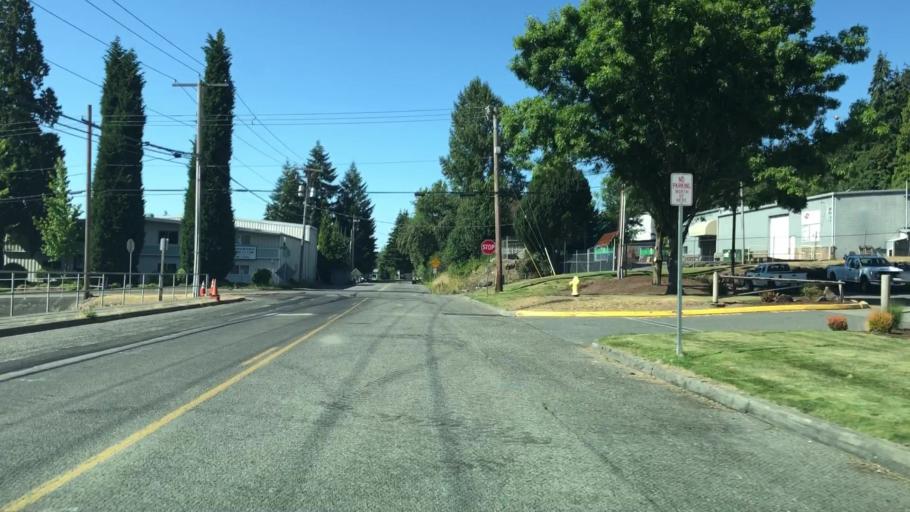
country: US
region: Washington
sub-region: King County
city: Woodinville
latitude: 47.7719
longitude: -122.1479
